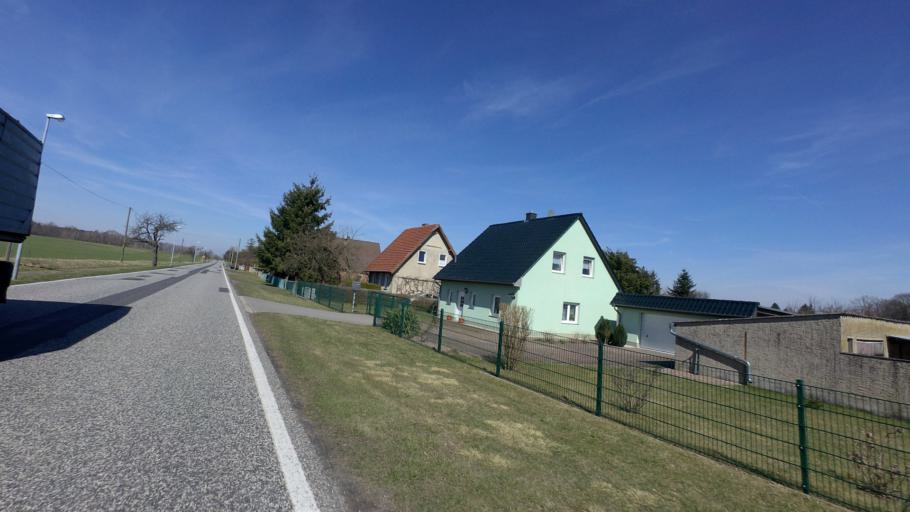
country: DE
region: Brandenburg
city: Furstenwalde
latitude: 52.4101
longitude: 14.0453
